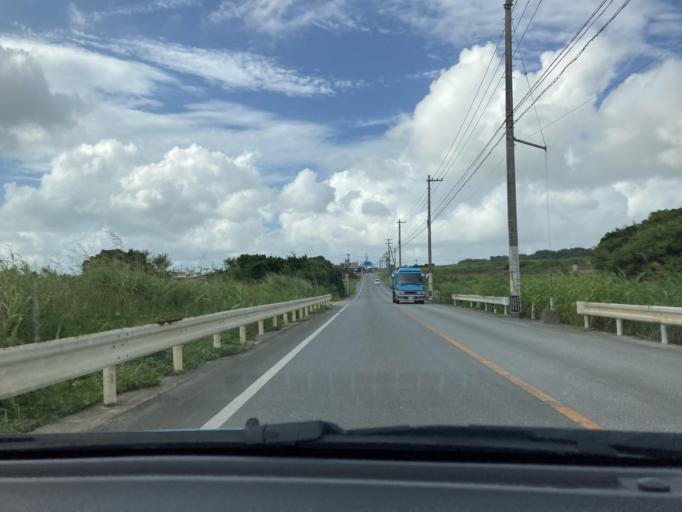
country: JP
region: Okinawa
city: Itoman
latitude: 26.0998
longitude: 127.6981
